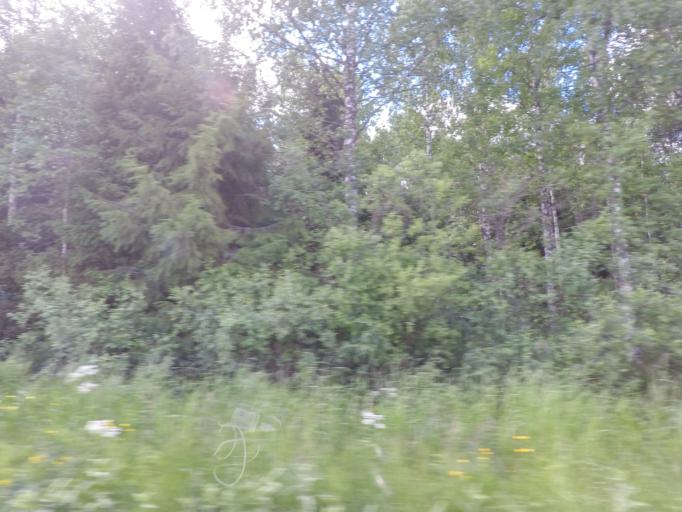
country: FI
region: Central Finland
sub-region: Jyvaeskylae
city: Hankasalmi
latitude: 62.4160
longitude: 26.6407
